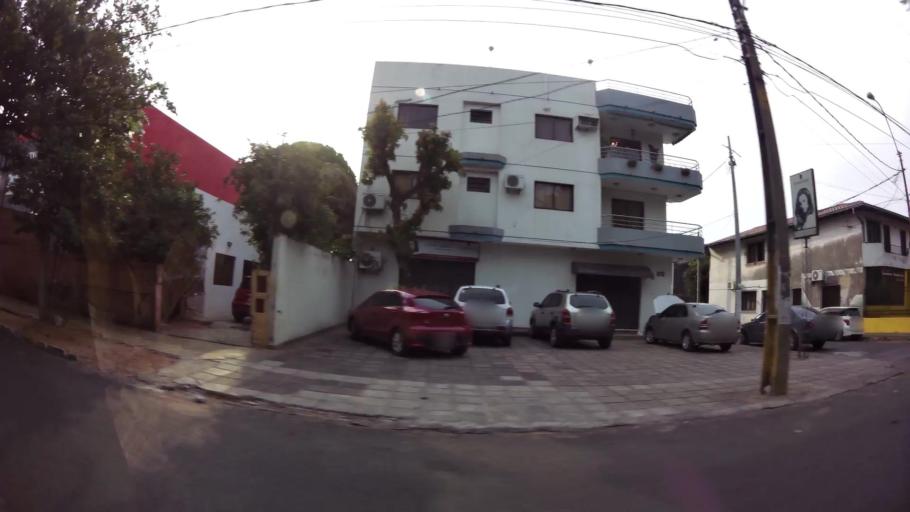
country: PY
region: Asuncion
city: Asuncion
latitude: -25.3069
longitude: -57.6085
